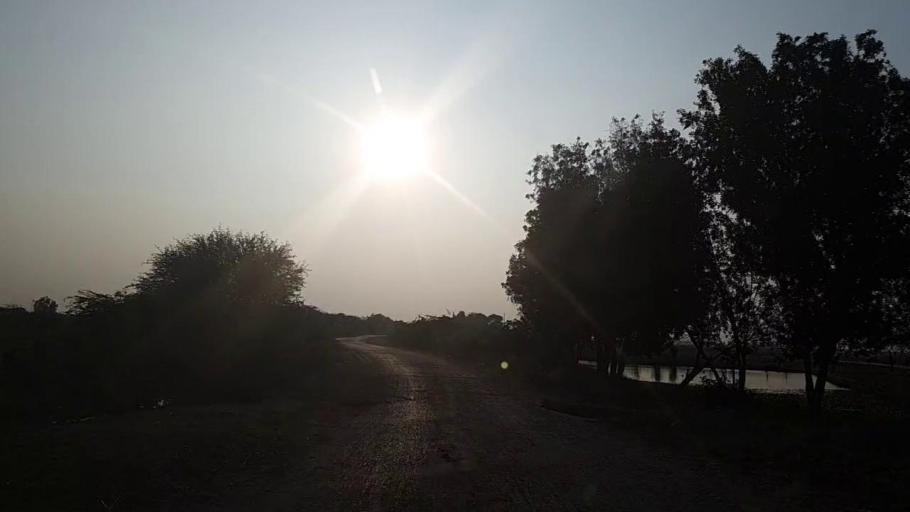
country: PK
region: Sindh
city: Mirpur Sakro
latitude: 24.5629
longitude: 67.6147
